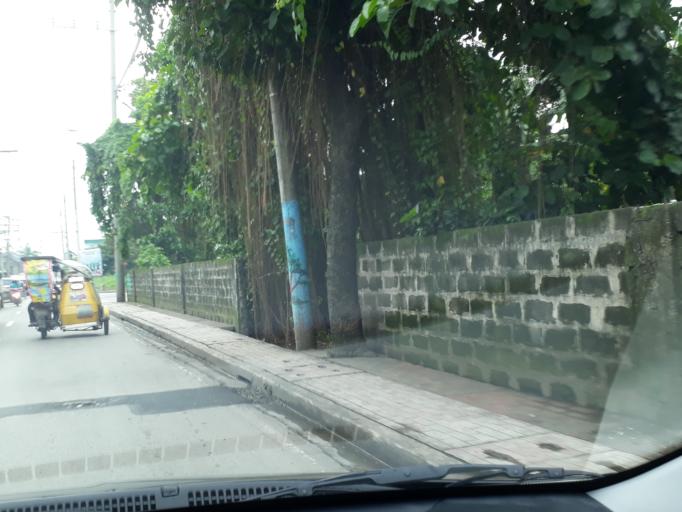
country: PH
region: Calabarzon
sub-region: Province of Rizal
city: Valenzuela
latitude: 14.7134
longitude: 120.9706
